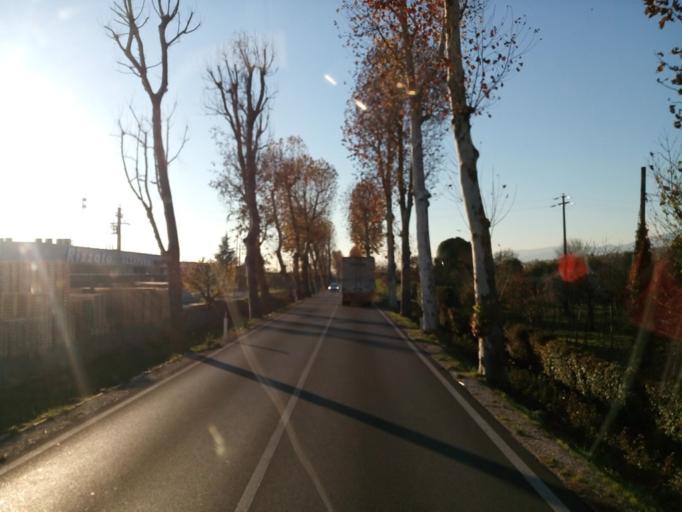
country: IT
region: Veneto
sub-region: Provincia di Treviso
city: Asolo
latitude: 45.7937
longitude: 11.9468
